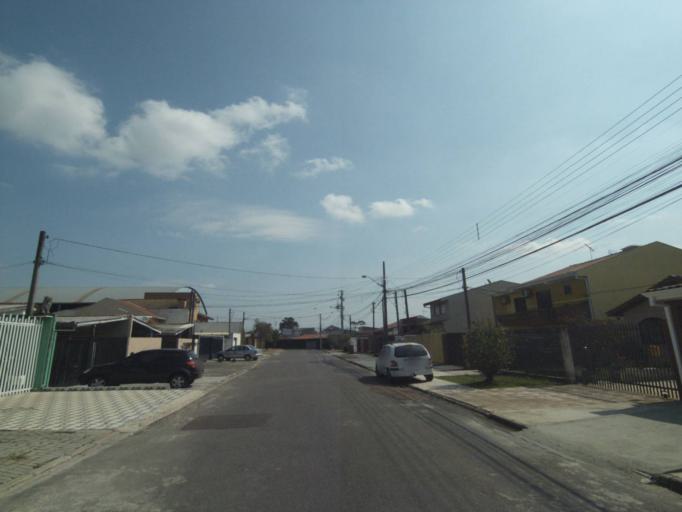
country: BR
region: Parana
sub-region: Curitiba
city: Curitiba
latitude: -25.4881
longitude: -49.3333
